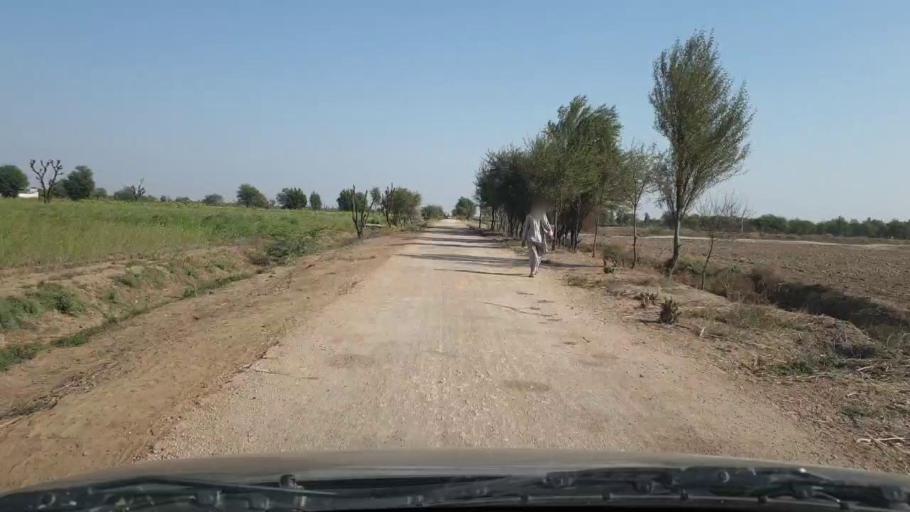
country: PK
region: Sindh
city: Samaro
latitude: 25.1920
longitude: 69.2846
